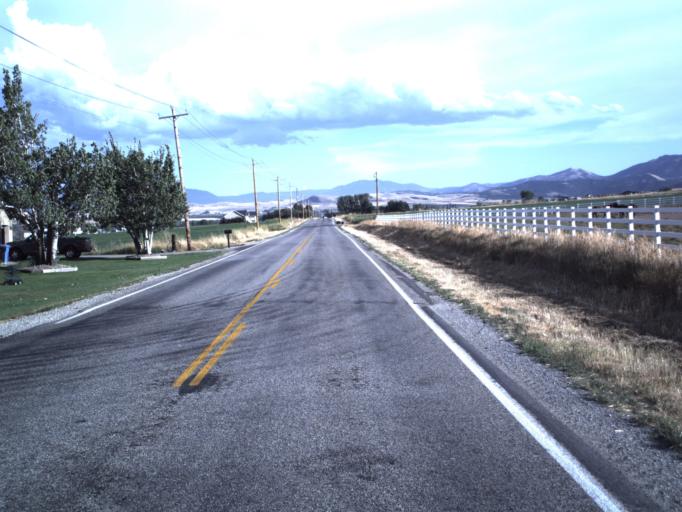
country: US
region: Utah
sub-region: Cache County
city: Wellsville
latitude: 41.6634
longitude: -111.9484
